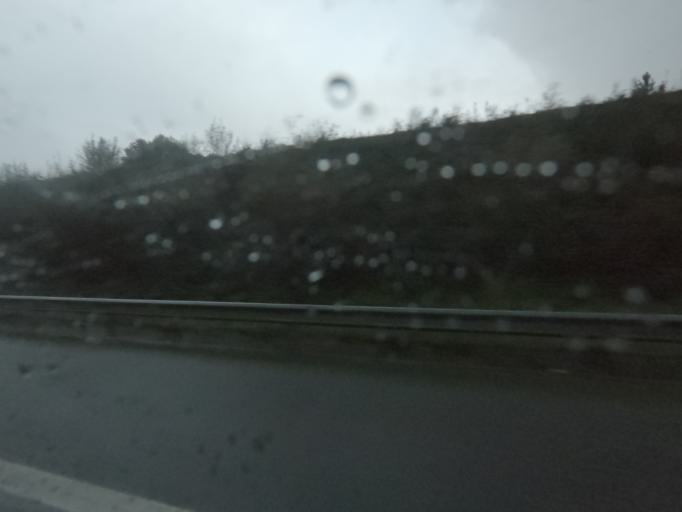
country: PT
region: Braga
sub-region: Braga
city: Braga
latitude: 41.5323
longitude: -8.4550
